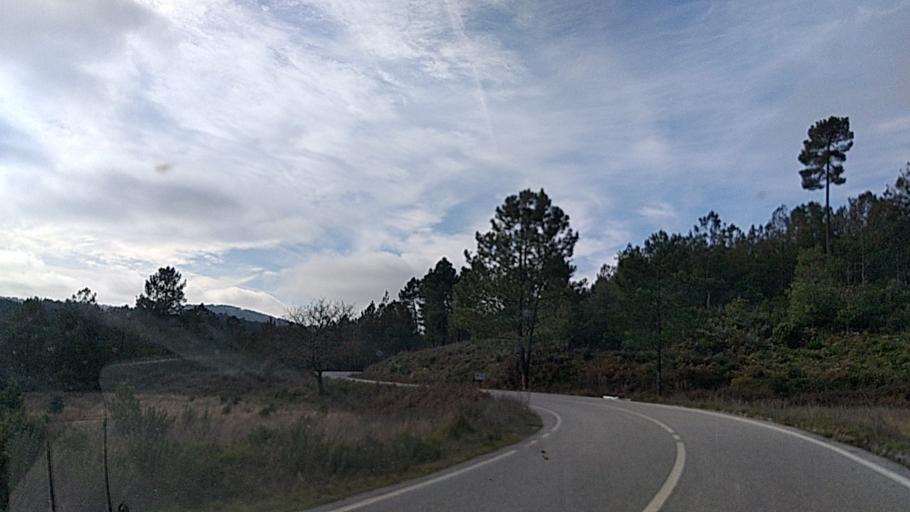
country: PT
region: Guarda
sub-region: Fornos de Algodres
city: Fornos de Algodres
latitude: 40.7141
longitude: -7.5633
